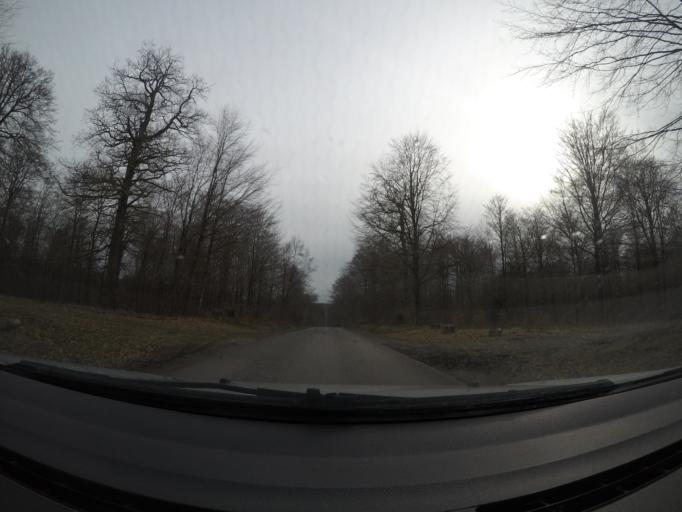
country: BE
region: Wallonia
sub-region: Province du Luxembourg
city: Martelange
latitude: 49.8000
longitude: 5.6977
